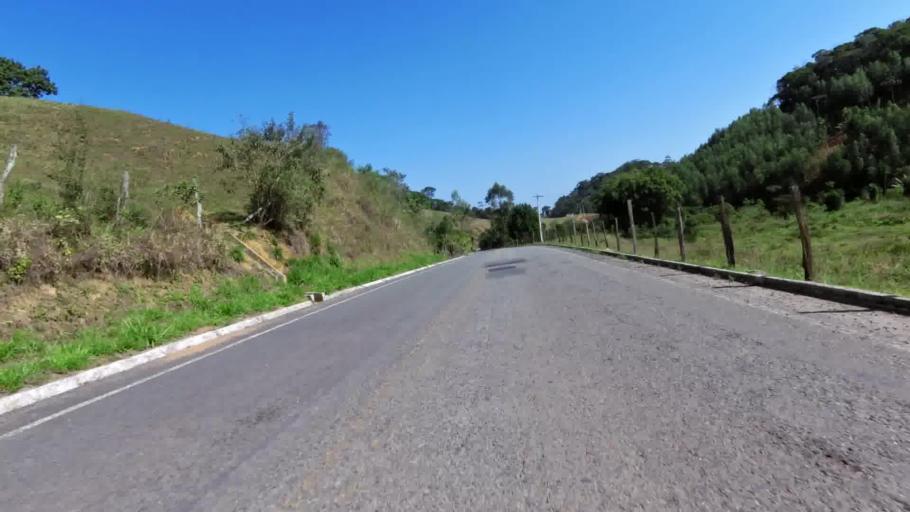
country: BR
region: Espirito Santo
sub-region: Alfredo Chaves
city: Alfredo Chaves
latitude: -20.5555
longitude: -40.7933
